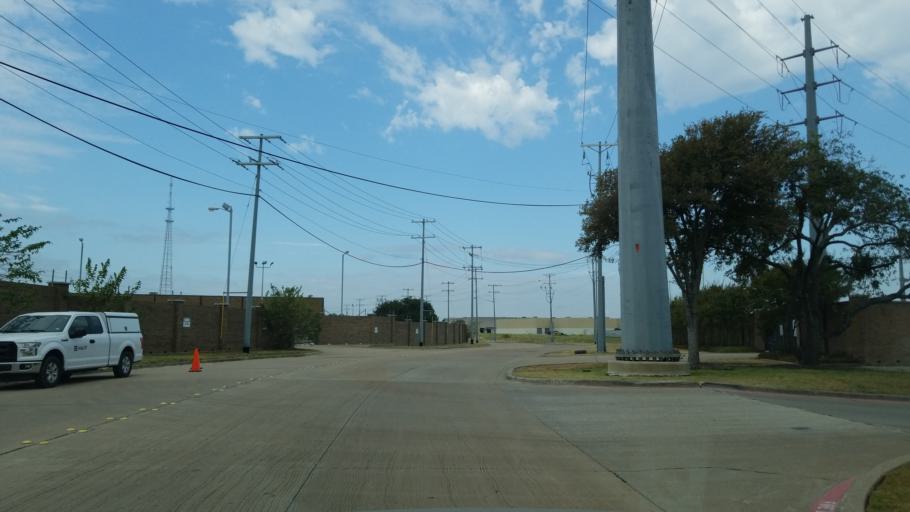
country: US
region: Texas
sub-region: Dallas County
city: Garland
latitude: 32.9012
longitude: -96.6770
